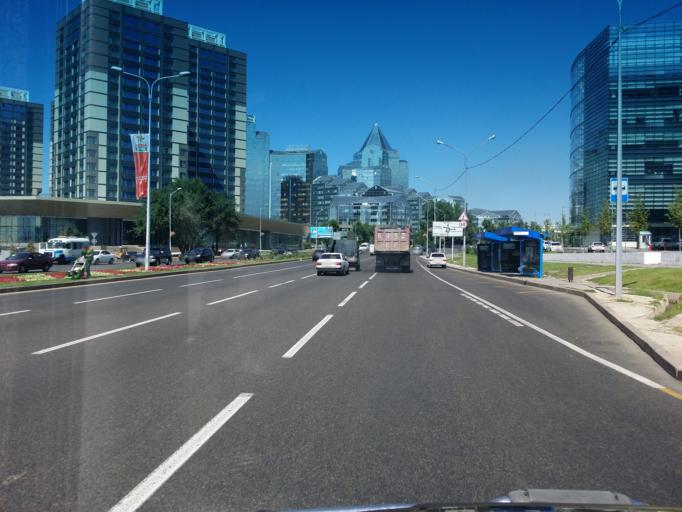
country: KZ
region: Almaty Qalasy
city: Almaty
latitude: 43.2267
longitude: 76.9422
